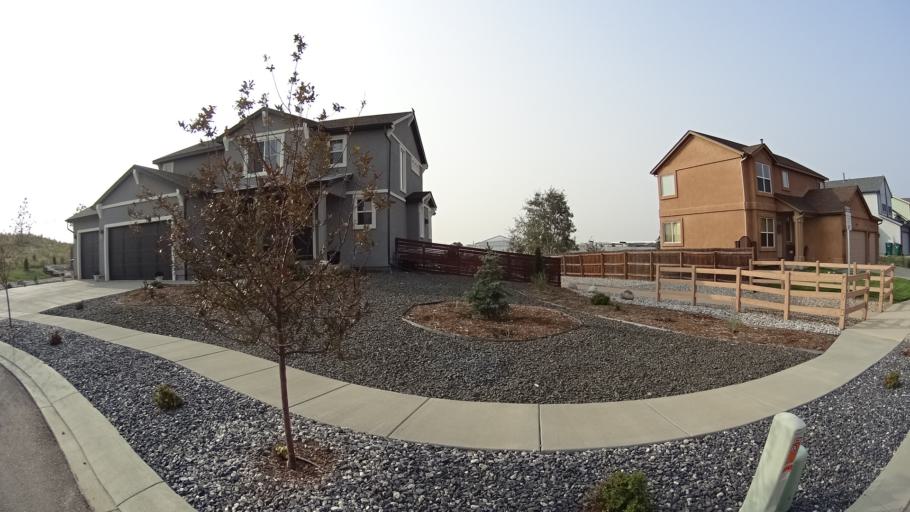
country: US
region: Colorado
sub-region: El Paso County
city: Cimarron Hills
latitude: 38.9318
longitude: -104.7211
